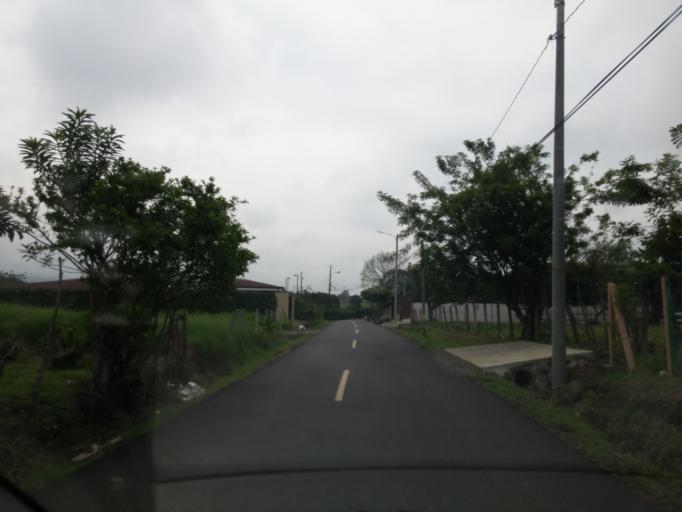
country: CR
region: Heredia
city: Mercedes
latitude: 10.0177
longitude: -84.1501
